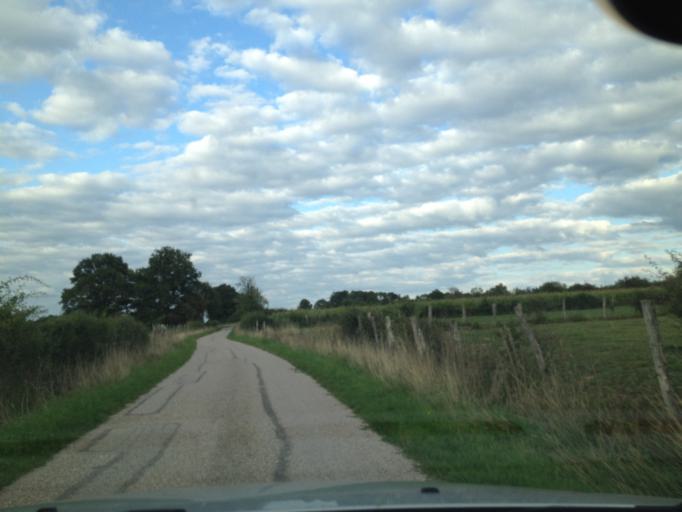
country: FR
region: Lorraine
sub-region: Departement des Vosges
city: Bains-les-Bains
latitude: 47.9809
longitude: 6.1826
